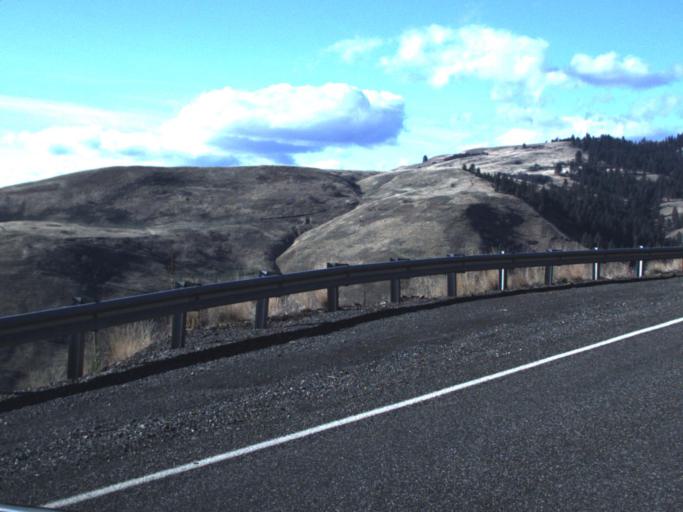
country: US
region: Washington
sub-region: Asotin County
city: Asotin
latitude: 46.0621
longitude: -117.2311
